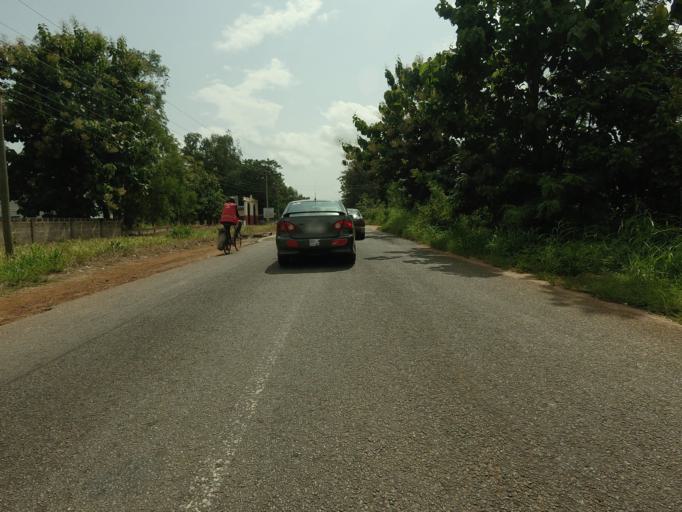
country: TG
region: Maritime
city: Lome
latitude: 6.2273
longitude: 1.0181
